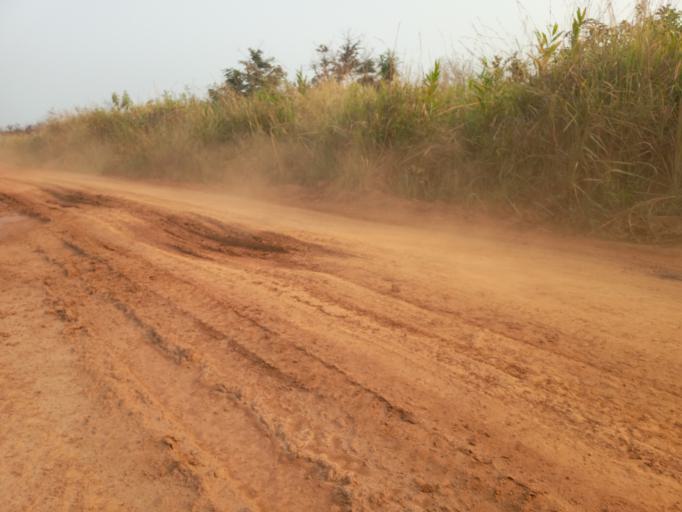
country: CD
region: Bandundu
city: Bandundu
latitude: -3.4118
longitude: 17.5987
